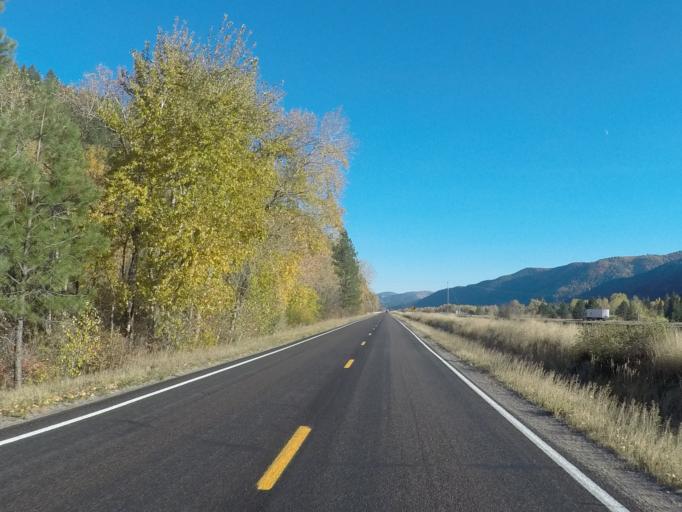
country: US
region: Montana
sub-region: Missoula County
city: Bonner-West Riverside
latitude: 46.8273
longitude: -113.8117
